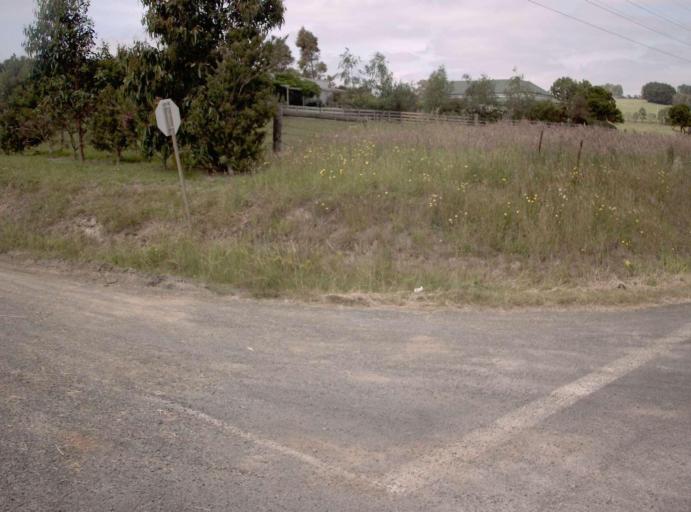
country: AU
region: Victoria
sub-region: Baw Baw
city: Warragul
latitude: -38.4434
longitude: 146.0305
